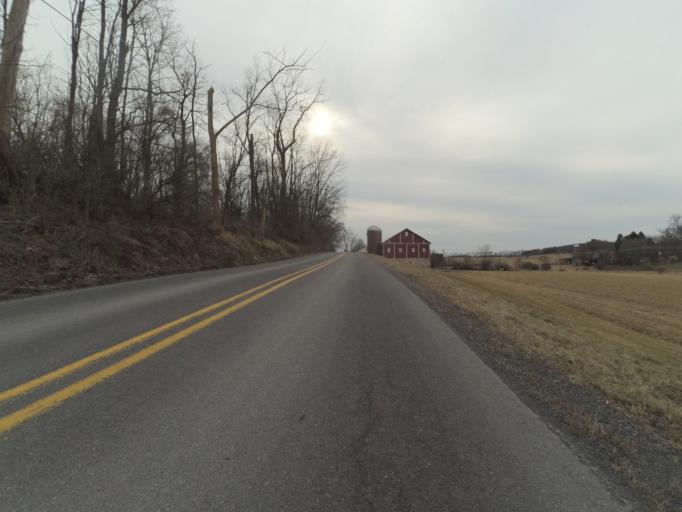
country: US
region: Pennsylvania
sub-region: Centre County
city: State College
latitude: 40.7715
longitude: -77.8350
